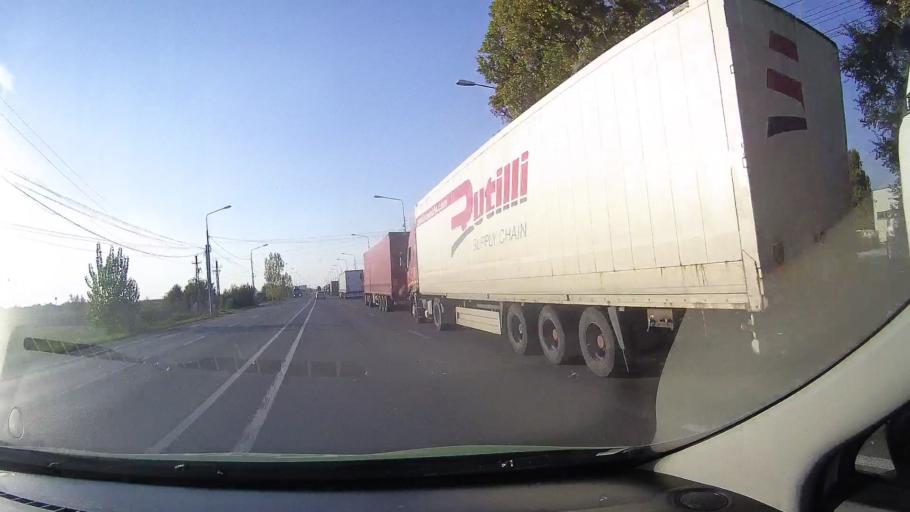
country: RO
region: Bihor
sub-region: Comuna Bors
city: Santion
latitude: 47.1025
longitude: 21.8387
